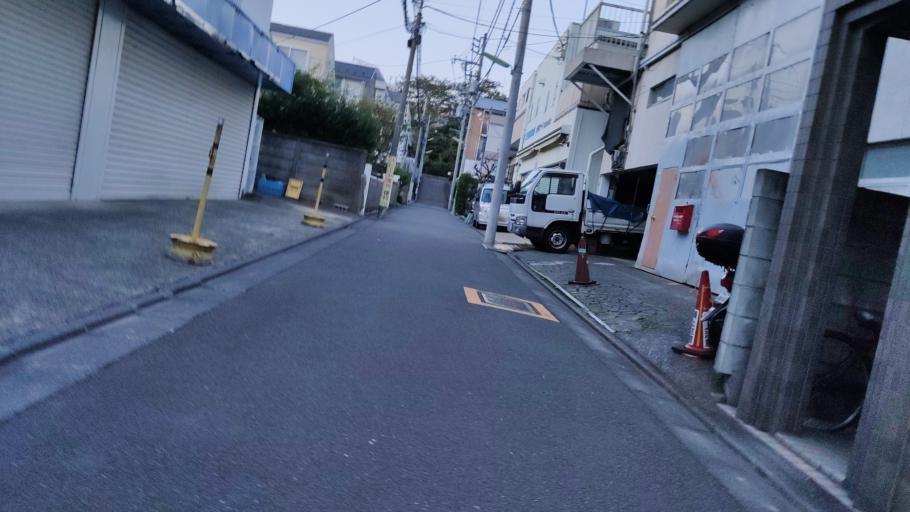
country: JP
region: Tokyo
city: Tokyo
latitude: 35.6558
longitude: 139.6804
